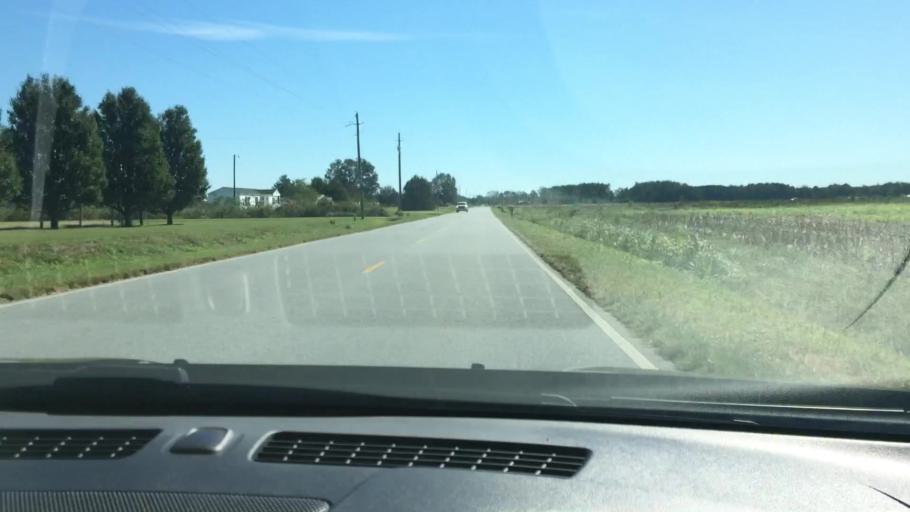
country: US
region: North Carolina
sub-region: Pitt County
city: Grifton
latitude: 35.3855
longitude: -77.3791
